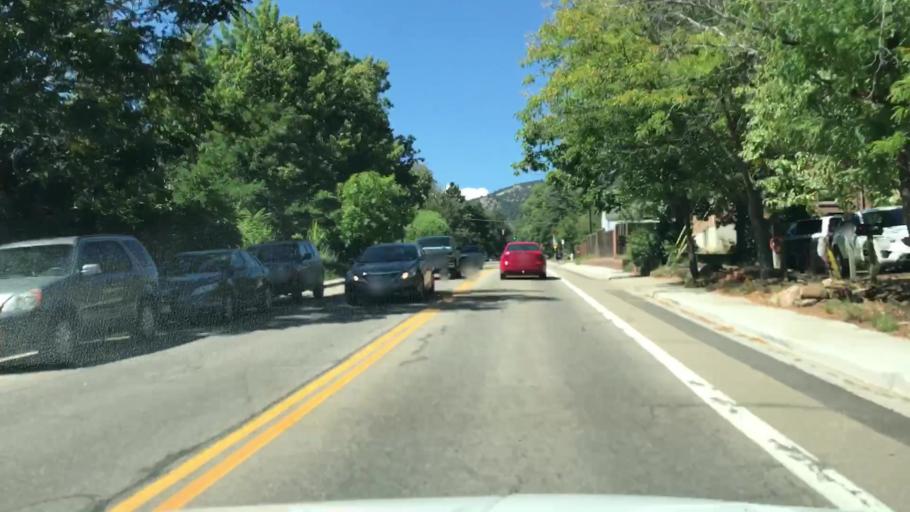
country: US
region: Colorado
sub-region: Boulder County
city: Boulder
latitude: 40.0001
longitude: -105.2691
